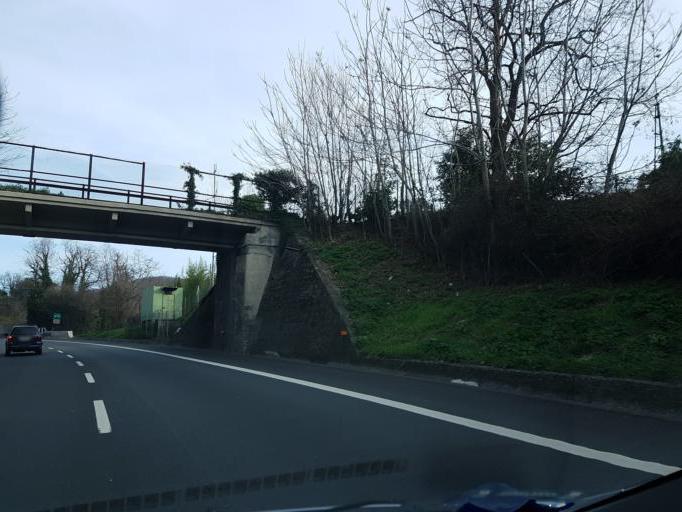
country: IT
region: Liguria
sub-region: Provincia di Genova
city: Manesseno
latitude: 44.4808
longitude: 8.9173
